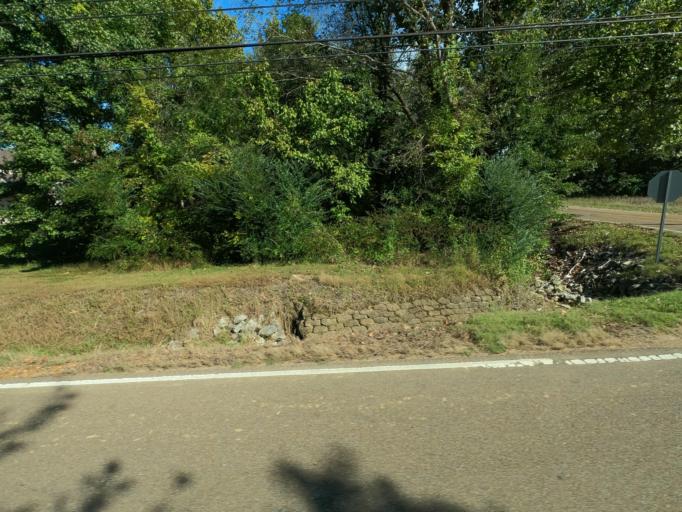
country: US
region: Tennessee
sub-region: Fayette County
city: Hickory Withe
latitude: 35.2327
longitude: -89.6500
